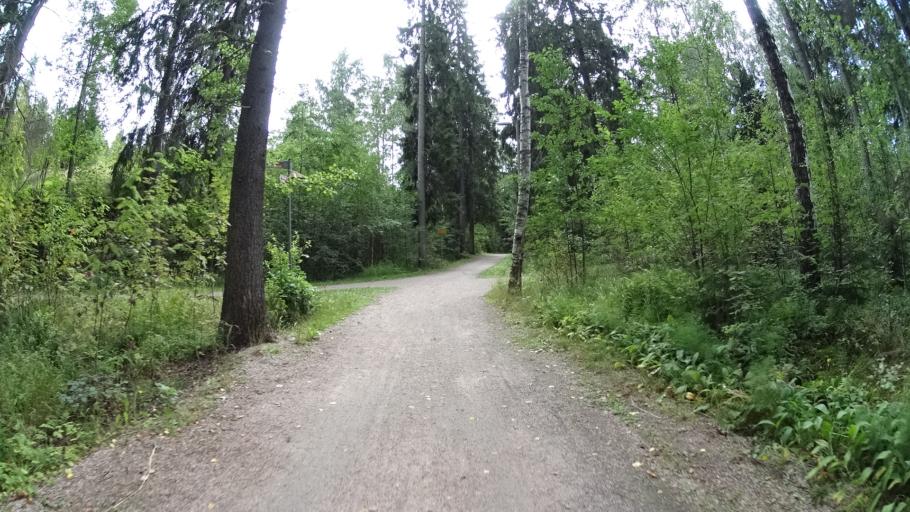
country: FI
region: Uusimaa
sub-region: Helsinki
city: Helsinki
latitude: 60.2624
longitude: 24.9026
